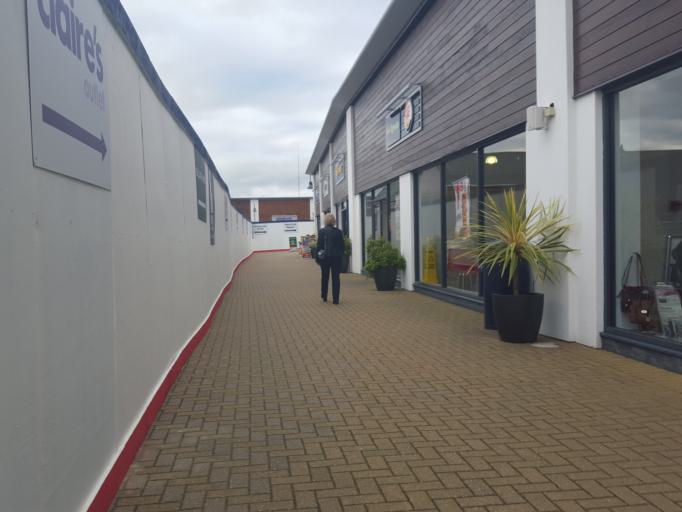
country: GB
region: England
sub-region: Essex
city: Little Clacton
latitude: 51.8186
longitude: 1.1688
